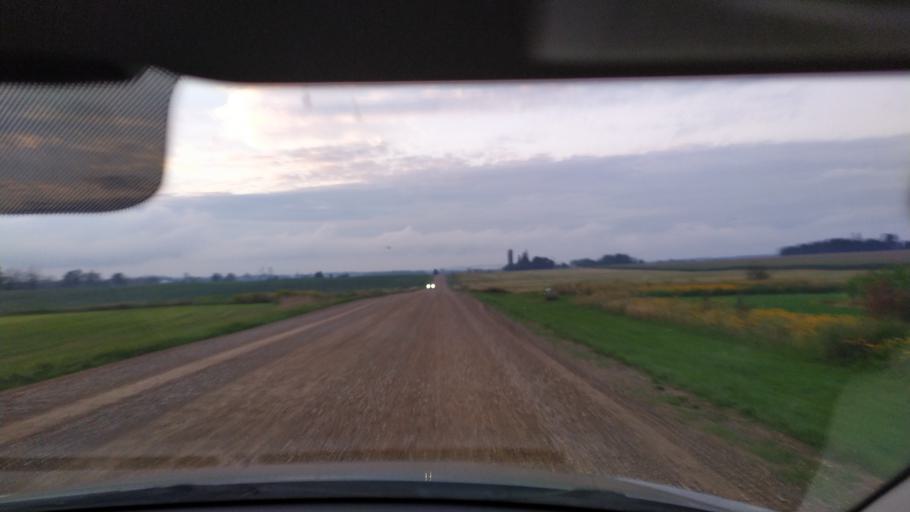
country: CA
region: Ontario
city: Kitchener
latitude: 43.3224
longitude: -80.6163
